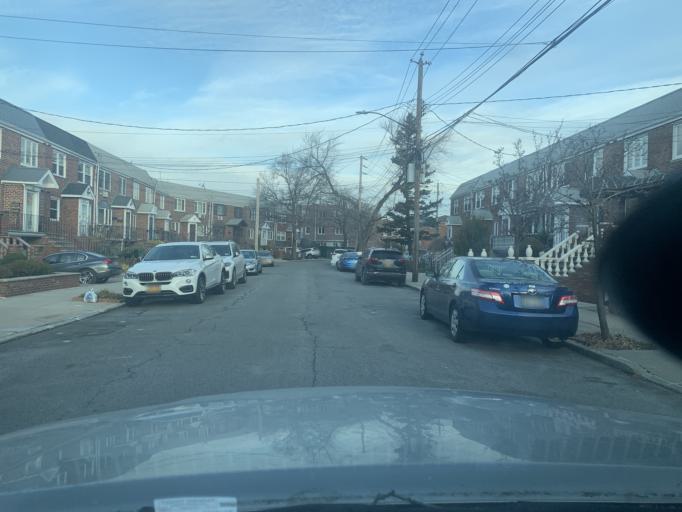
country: US
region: New York
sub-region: Kings County
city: East New York
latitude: 40.7236
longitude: -73.8858
